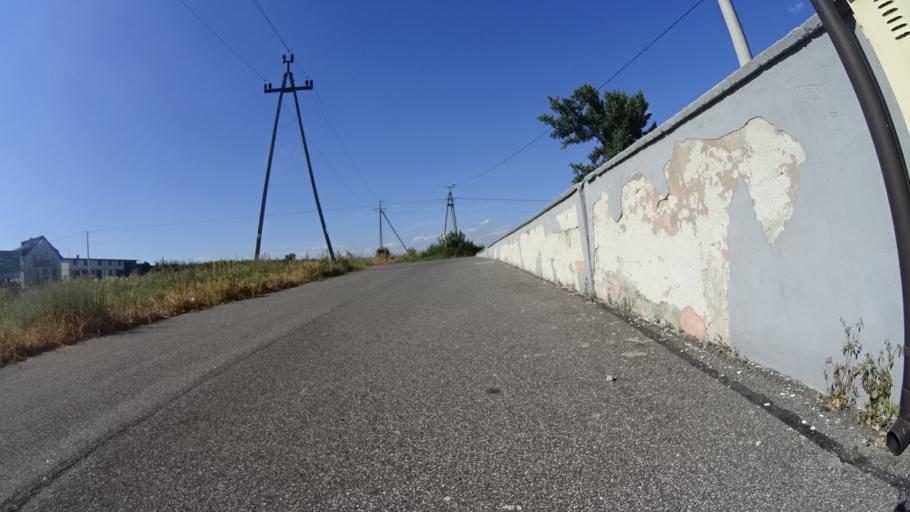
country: PL
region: Masovian Voivodeship
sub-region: Powiat bialobrzeski
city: Wysmierzyce
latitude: 51.6643
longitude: 20.8593
